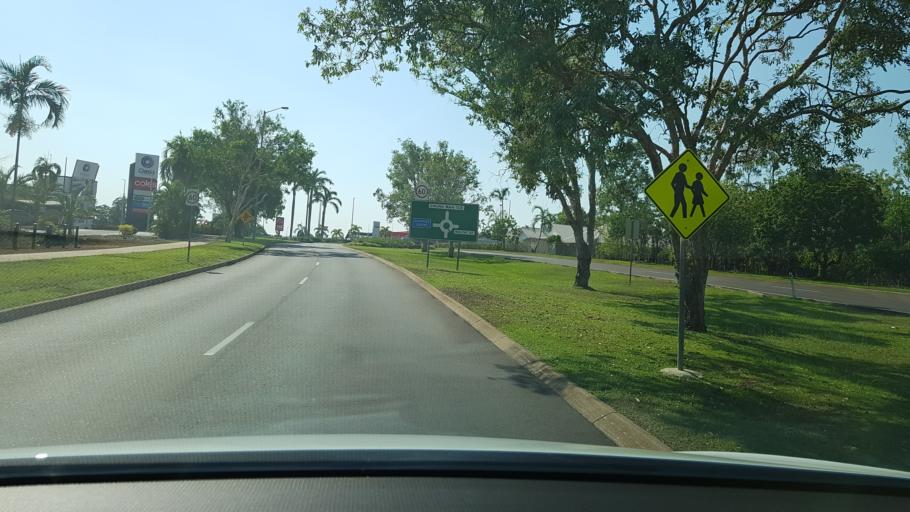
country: AU
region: Northern Territory
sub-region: Palmerston
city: Palmerston
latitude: -12.4844
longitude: 130.9872
